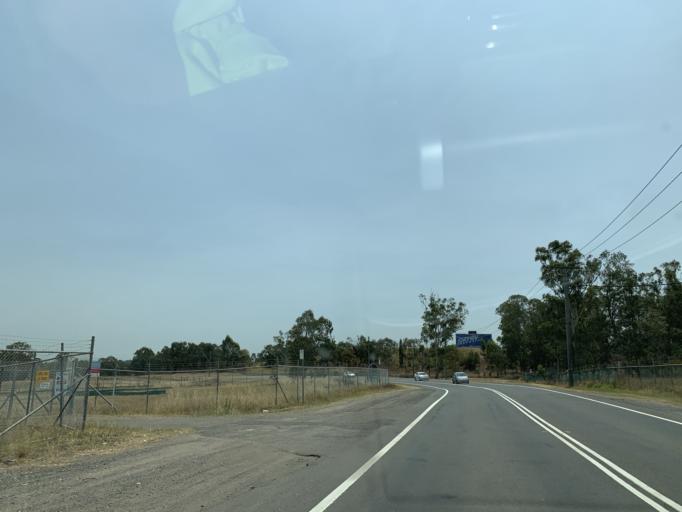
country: AU
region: New South Wales
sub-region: Fairfield
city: Horsley Park
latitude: -33.8239
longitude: 150.8709
